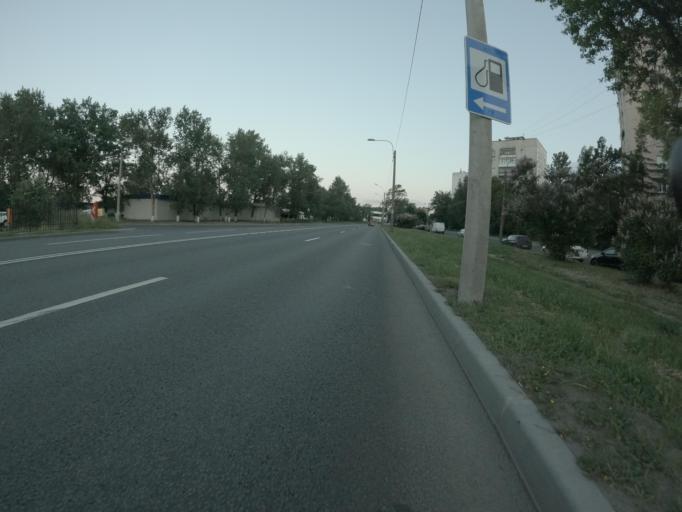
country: RU
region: St.-Petersburg
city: Dachnoye
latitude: 59.8472
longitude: 30.2802
